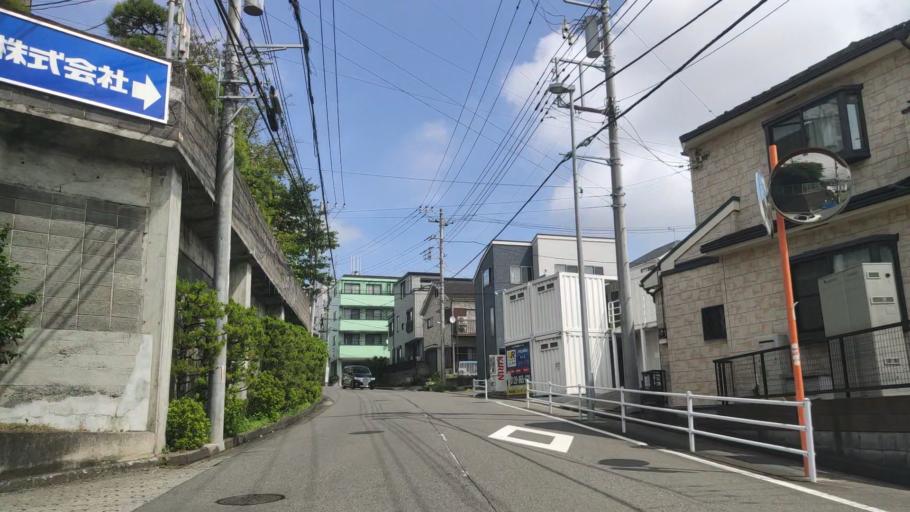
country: JP
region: Kanagawa
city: Minami-rinkan
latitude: 35.4239
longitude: 139.5359
